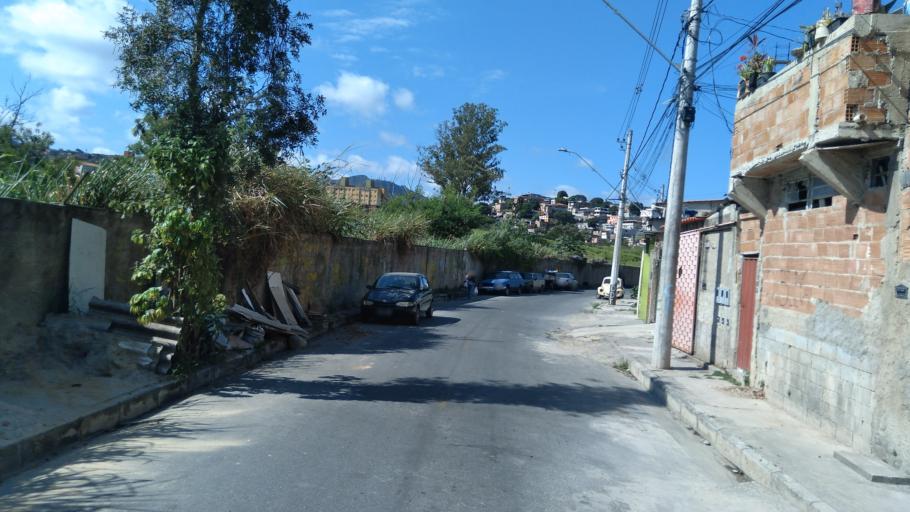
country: BR
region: Minas Gerais
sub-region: Belo Horizonte
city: Belo Horizonte
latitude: -19.9035
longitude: -43.8870
